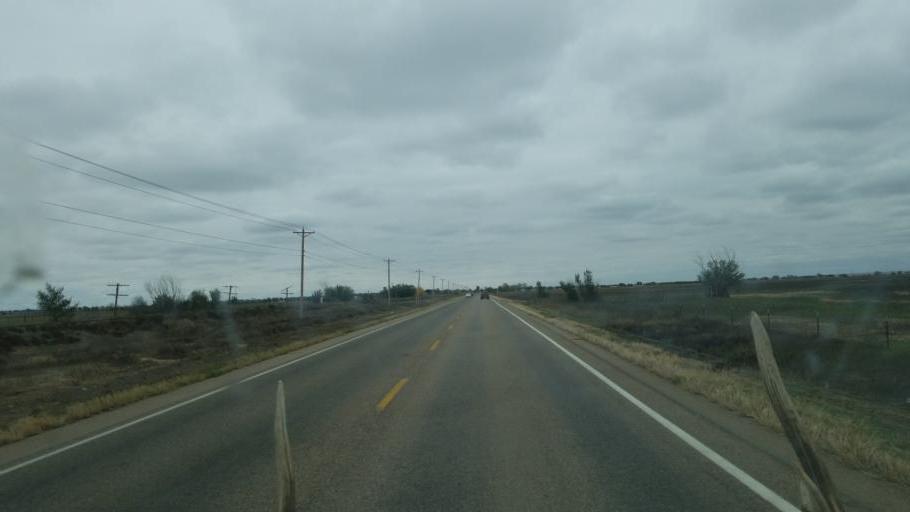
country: US
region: Colorado
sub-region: Crowley County
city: Ordway
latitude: 38.2071
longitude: -103.7965
